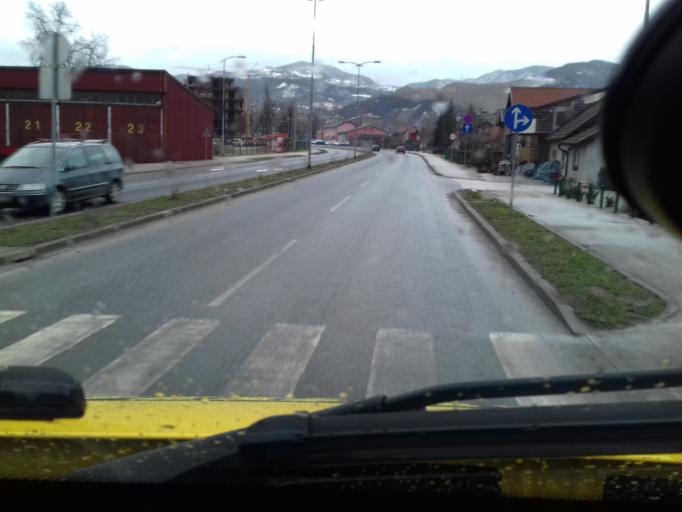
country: BA
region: Federation of Bosnia and Herzegovina
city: Zenica
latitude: 44.2069
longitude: 17.9019
